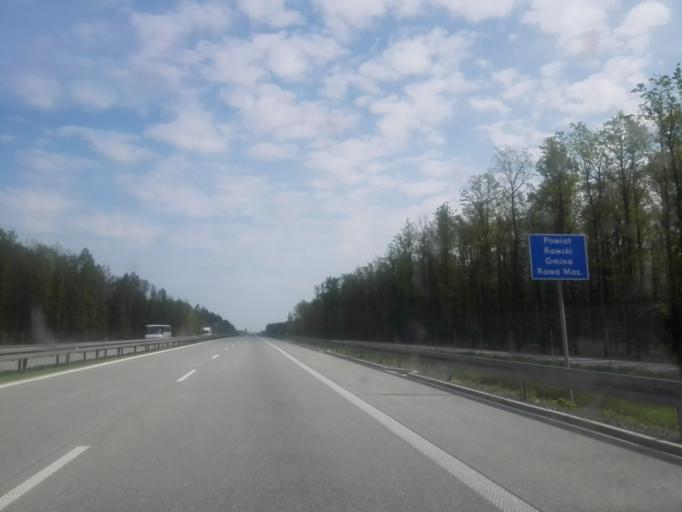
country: PL
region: Lodz Voivodeship
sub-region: Powiat rawski
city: Rawa Mazowiecka
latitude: 51.7212
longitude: 20.2234
